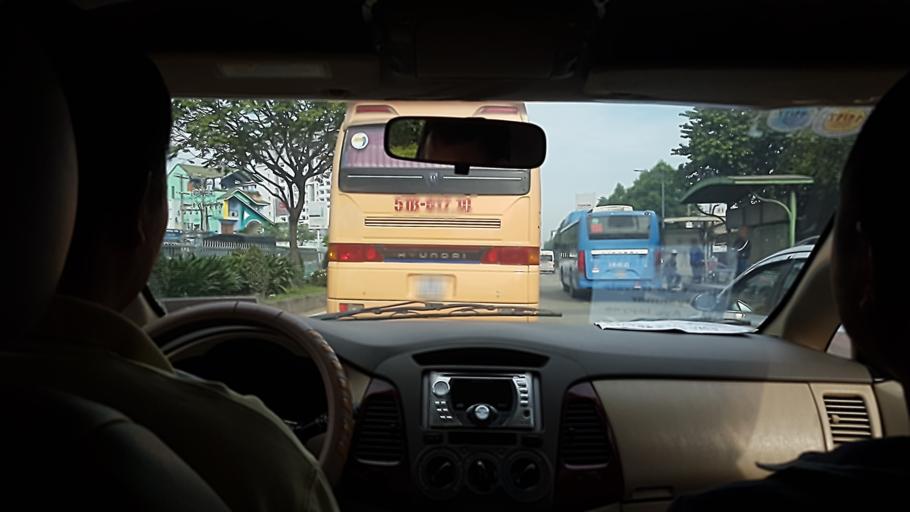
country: VN
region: Ho Chi Minh City
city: Ho Chi Minh City
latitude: 10.8282
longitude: 106.6247
